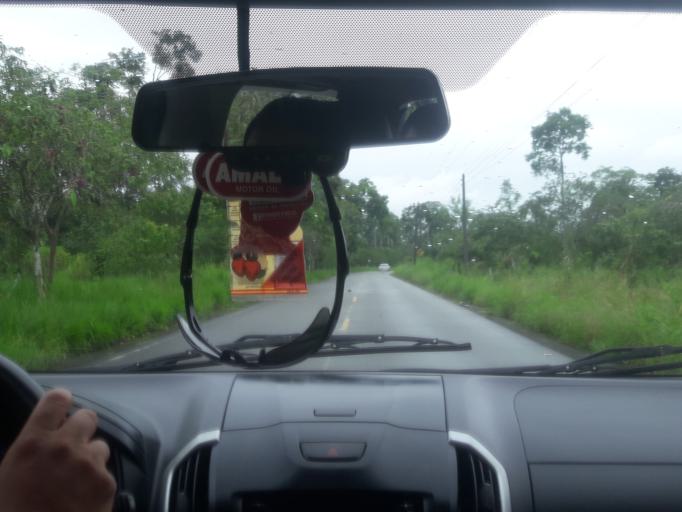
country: EC
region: Napo
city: Tena
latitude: -1.0341
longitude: -77.6791
